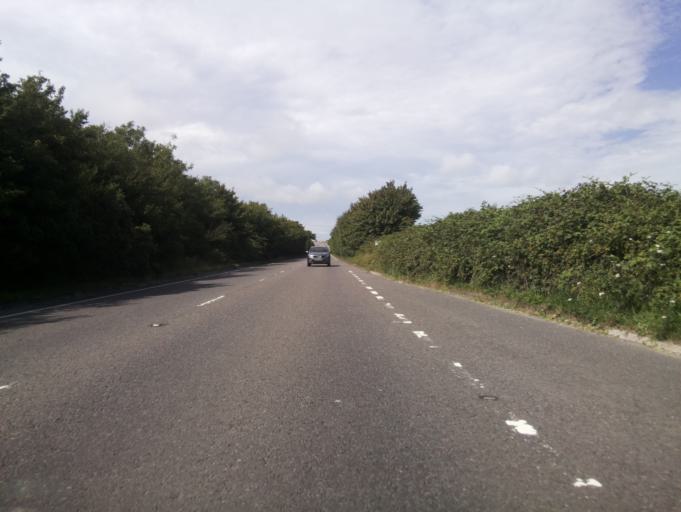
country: GB
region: England
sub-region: Dorset
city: Dorchester
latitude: 50.7739
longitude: -2.5390
